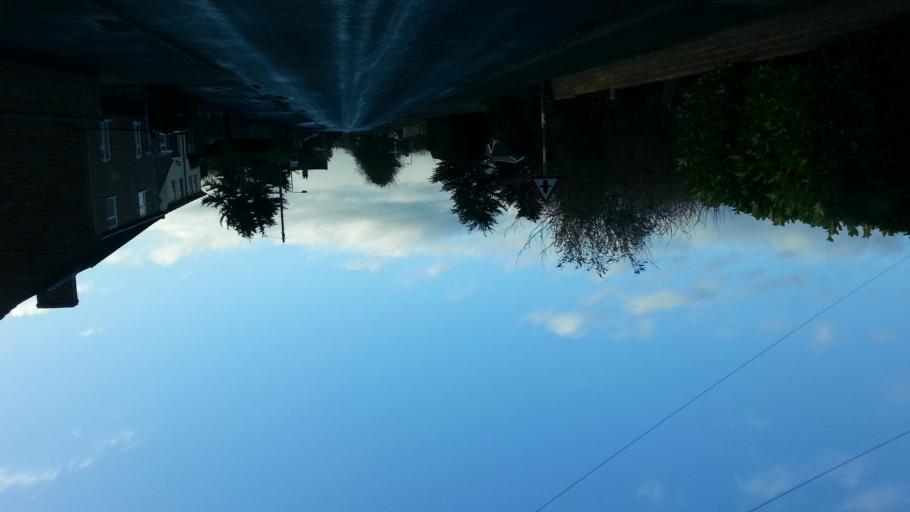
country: GB
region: England
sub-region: Norfolk
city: Ditchingham
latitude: 52.4679
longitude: 1.4427
